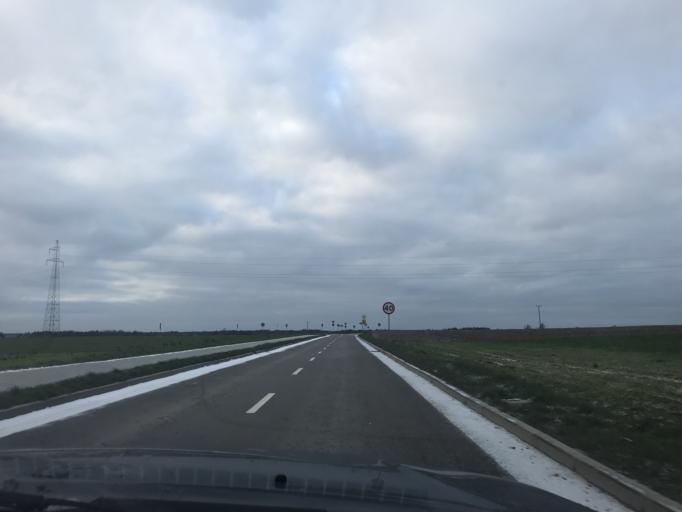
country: PL
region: Pomeranian Voivodeship
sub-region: Powiat chojnicki
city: Brusy
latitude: 53.8724
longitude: 17.7525
